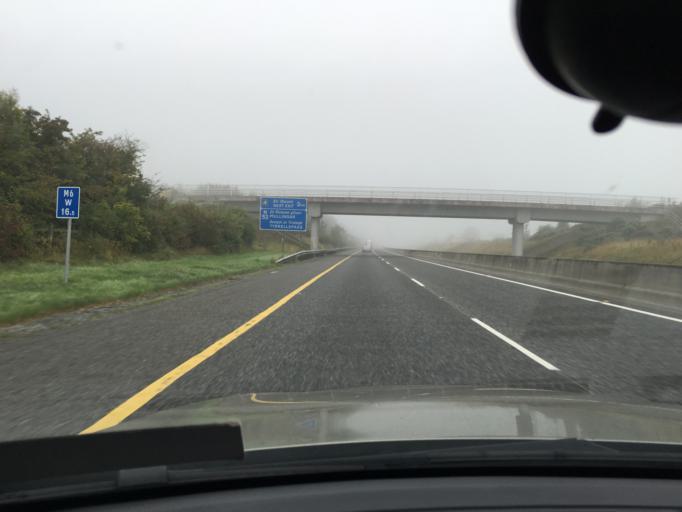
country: IE
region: Leinster
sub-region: An Iarmhi
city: Rochfortbridge
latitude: 53.3979
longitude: -7.3140
